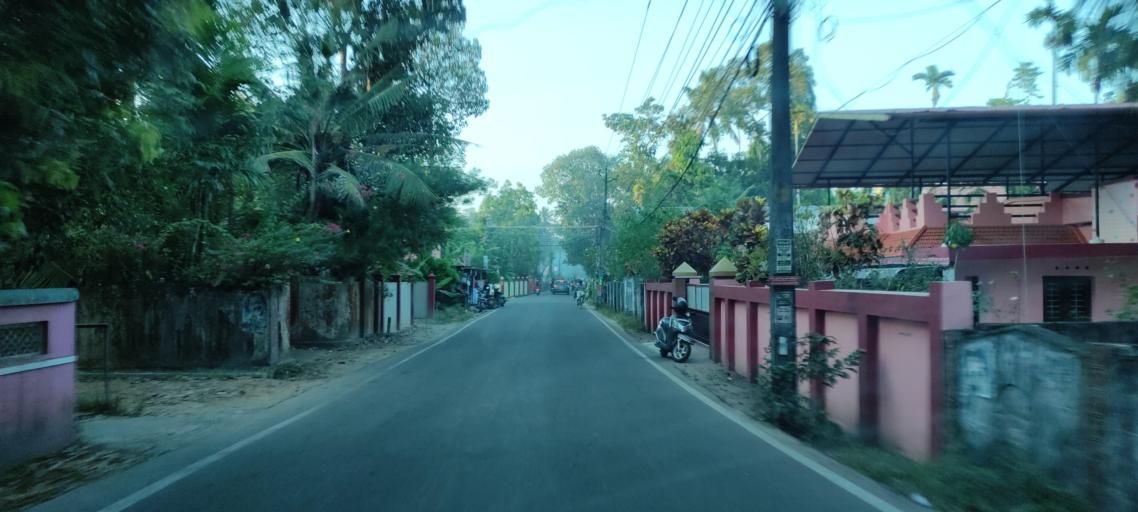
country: IN
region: Kerala
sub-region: Alappuzha
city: Kayankulam
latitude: 9.2457
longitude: 76.4528
